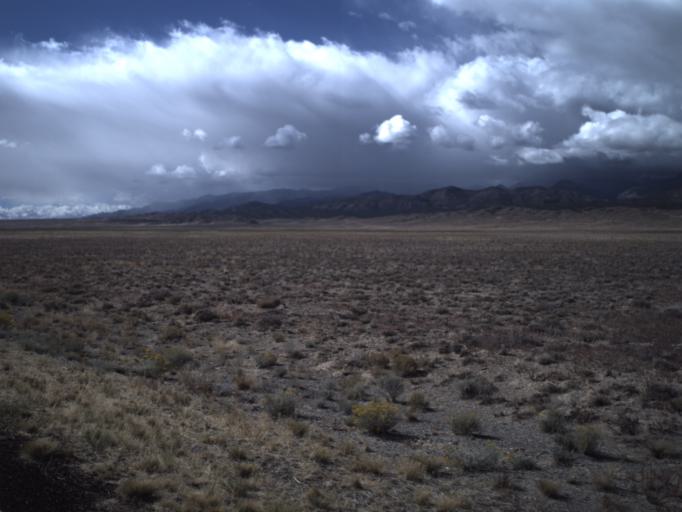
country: US
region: Nevada
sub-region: White Pine County
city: McGill
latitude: 38.9823
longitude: -114.0342
